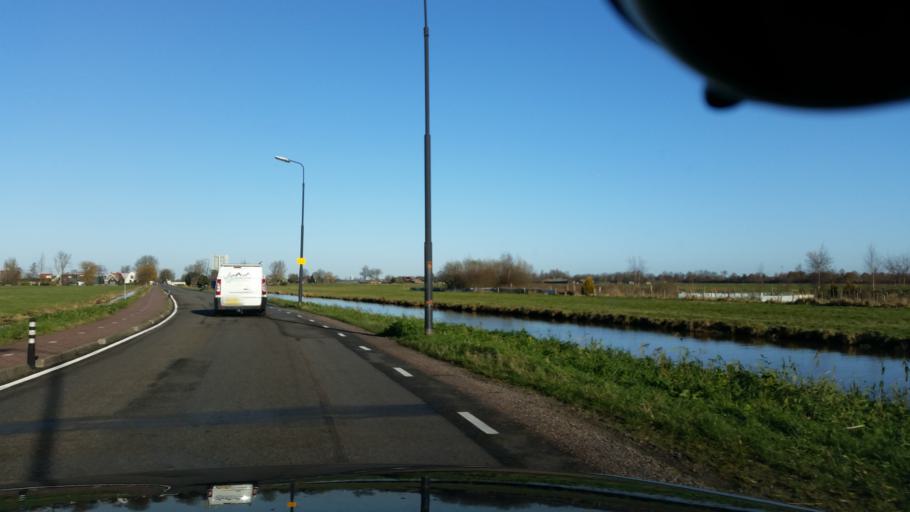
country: NL
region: Utrecht
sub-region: Gemeente De Ronde Venen
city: Mijdrecht
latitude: 52.2168
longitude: 4.9041
